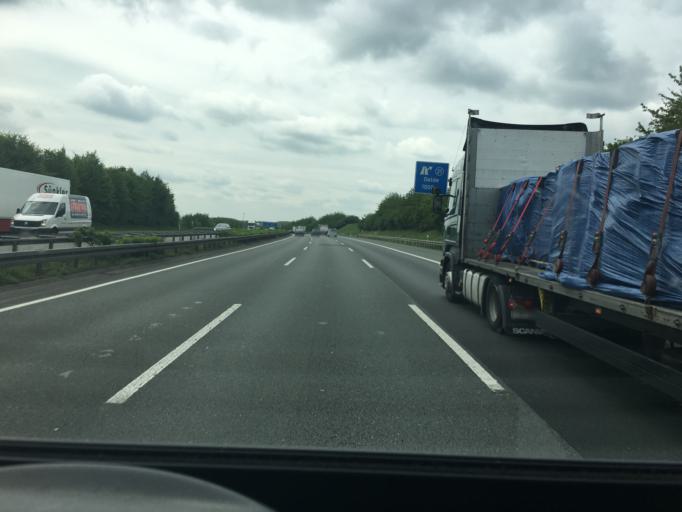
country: DE
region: North Rhine-Westphalia
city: Oelde
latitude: 51.8128
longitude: 8.1467
